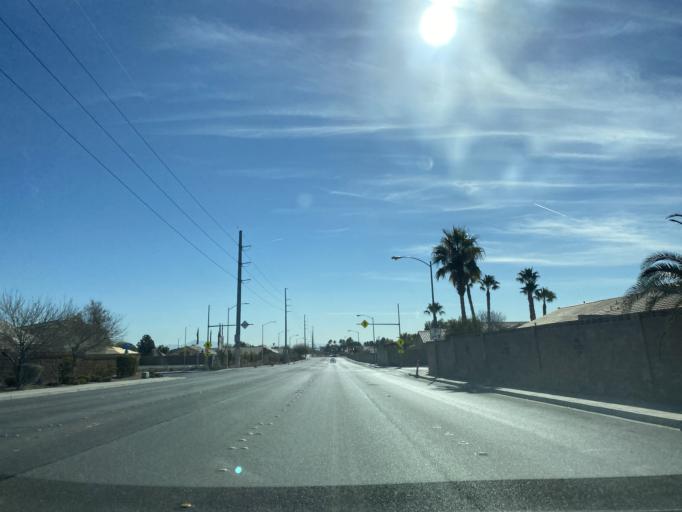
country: US
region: Nevada
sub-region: Clark County
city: North Las Vegas
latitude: 36.2511
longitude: -115.1441
